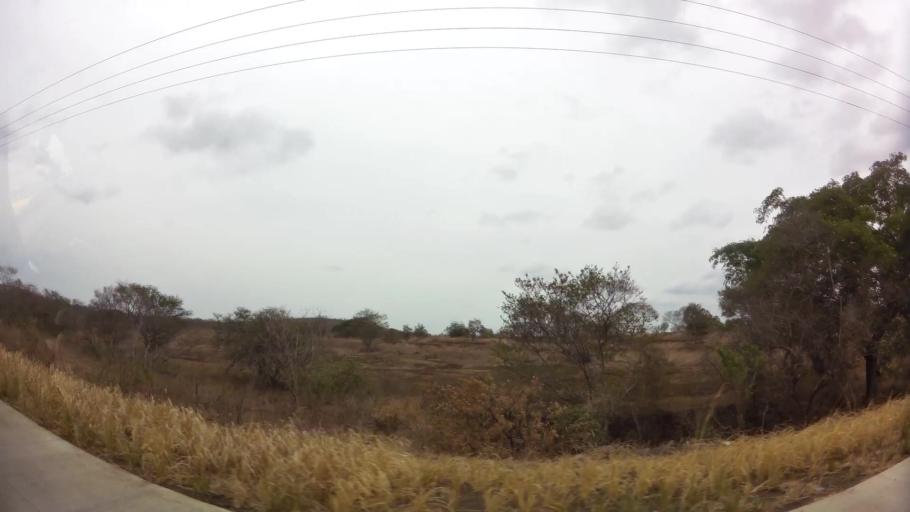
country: NI
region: Masaya
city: Ticuantepe
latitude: 12.0949
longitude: -86.1783
